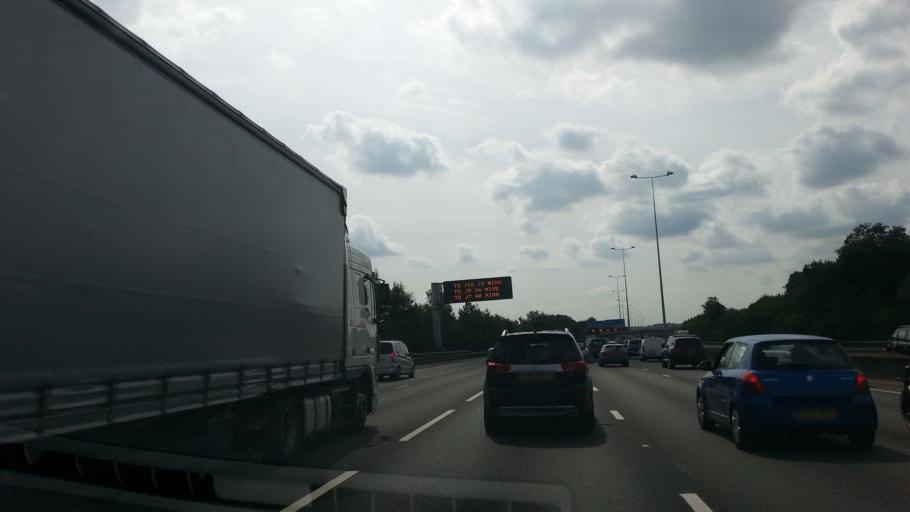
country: GB
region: England
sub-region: Surrey
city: Egham
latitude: 51.4189
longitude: -0.5395
